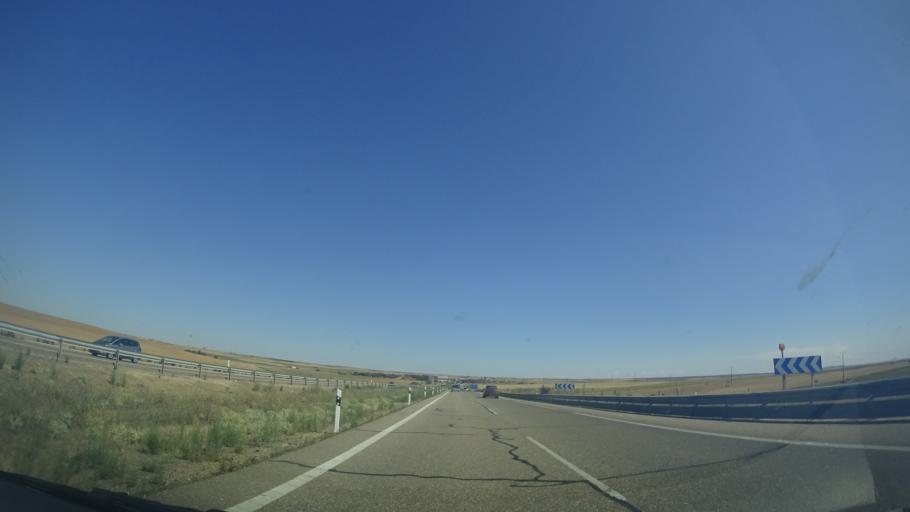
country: ES
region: Castille and Leon
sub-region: Provincia de Zamora
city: Cerecinos de Campos
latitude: 41.9117
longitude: -5.5054
